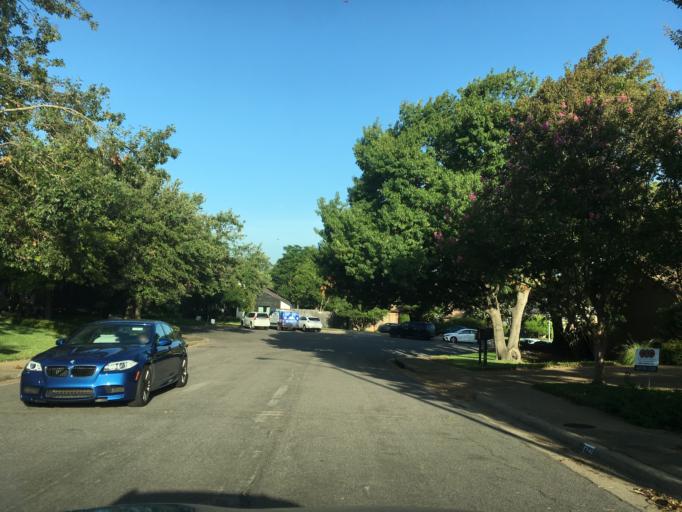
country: US
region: Texas
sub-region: Dallas County
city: Richardson
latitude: 32.8896
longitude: -96.7404
